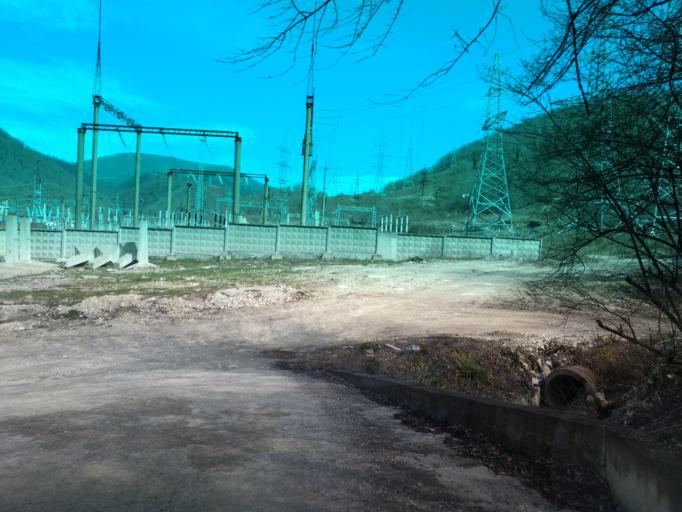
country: RU
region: Krasnodarskiy
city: Shepsi
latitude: 44.0527
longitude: 39.1640
